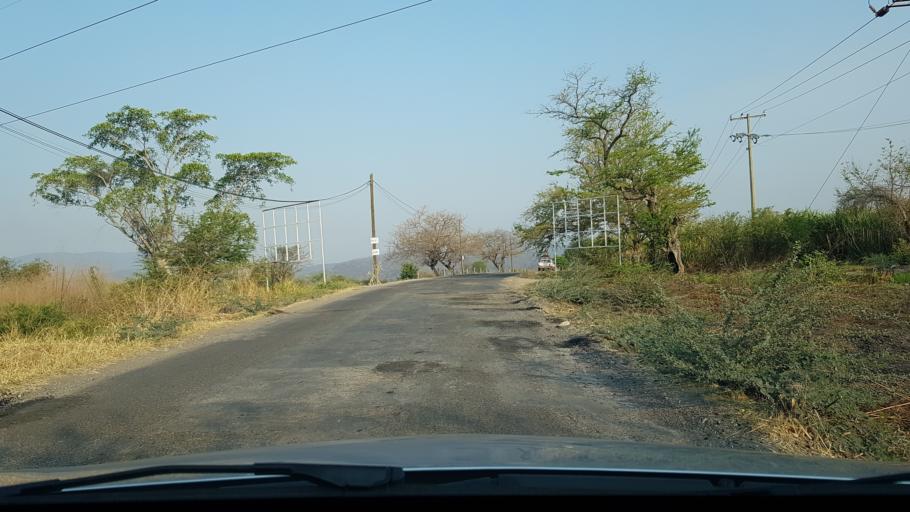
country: MX
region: Morelos
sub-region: Tepalcingo
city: Zacapalco
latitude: 18.6285
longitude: -99.0077
